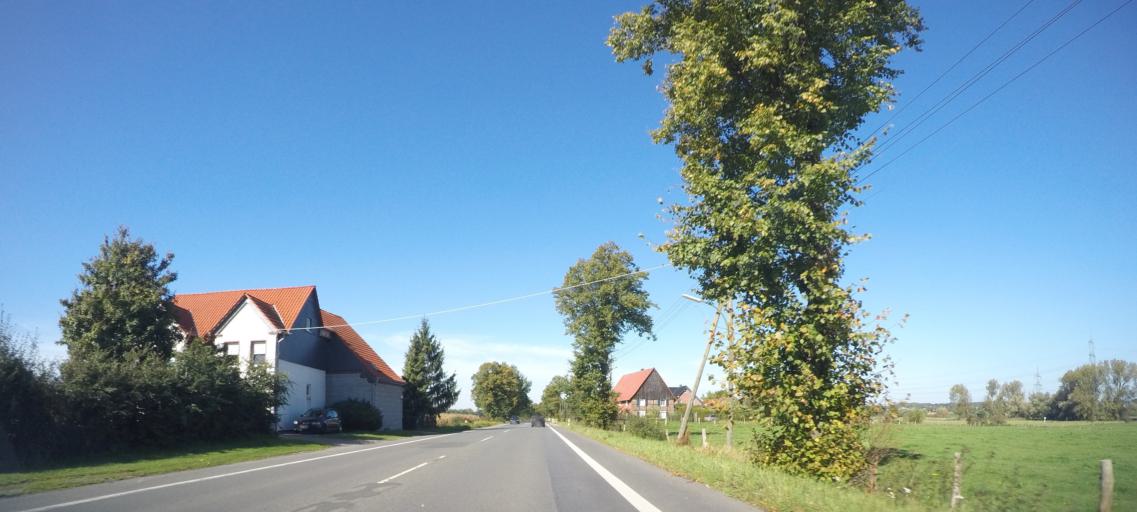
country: DE
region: North Rhine-Westphalia
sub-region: Regierungsbezirk Arnsberg
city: Welver
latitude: 51.6955
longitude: 7.9402
